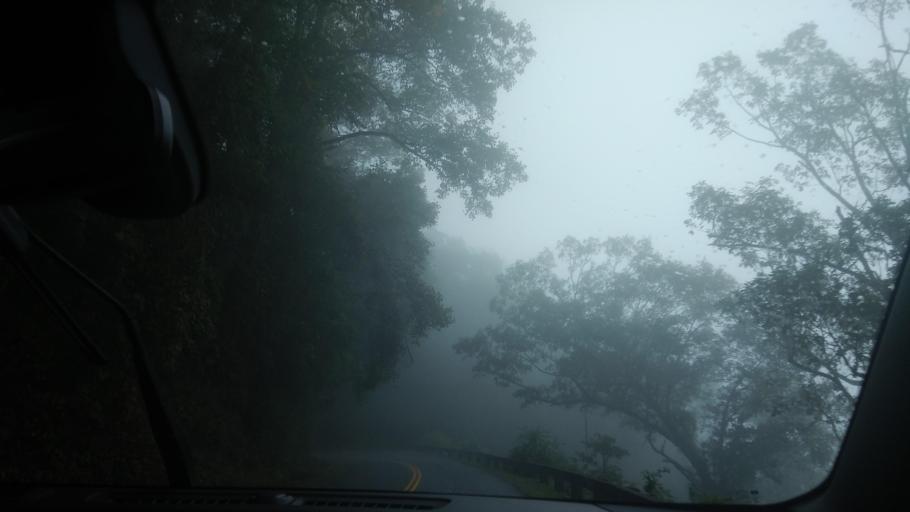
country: US
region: North Carolina
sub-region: Mitchell County
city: Spruce Pine
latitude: 35.8805
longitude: -81.9868
